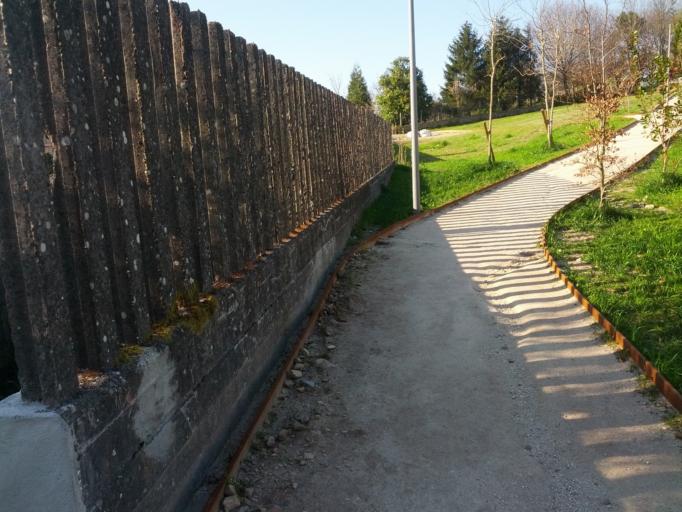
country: ES
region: Galicia
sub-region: Provincia da Coruna
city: Santiago de Compostela
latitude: 42.8850
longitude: -8.5373
